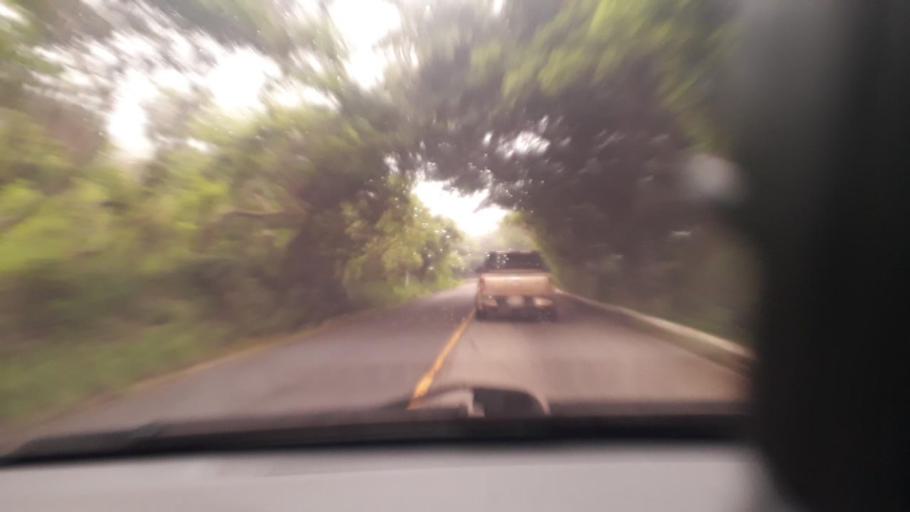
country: GT
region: Jutiapa
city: Jalpatagua
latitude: 14.1820
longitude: -90.0380
